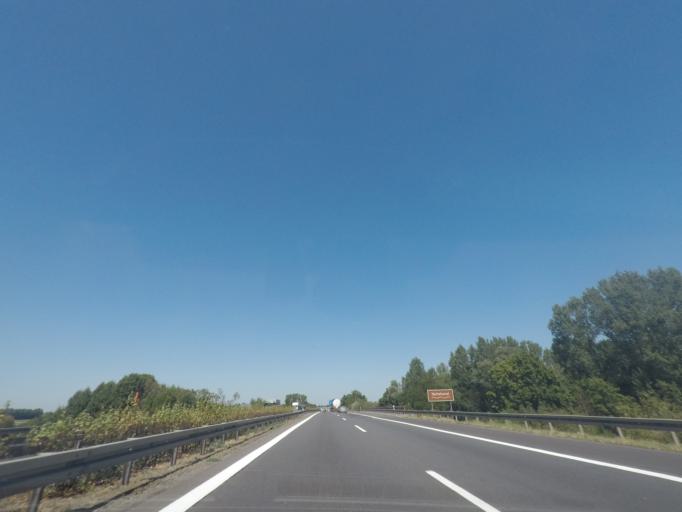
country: DE
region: Brandenburg
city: Mittenwalde
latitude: 52.2801
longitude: 13.5674
